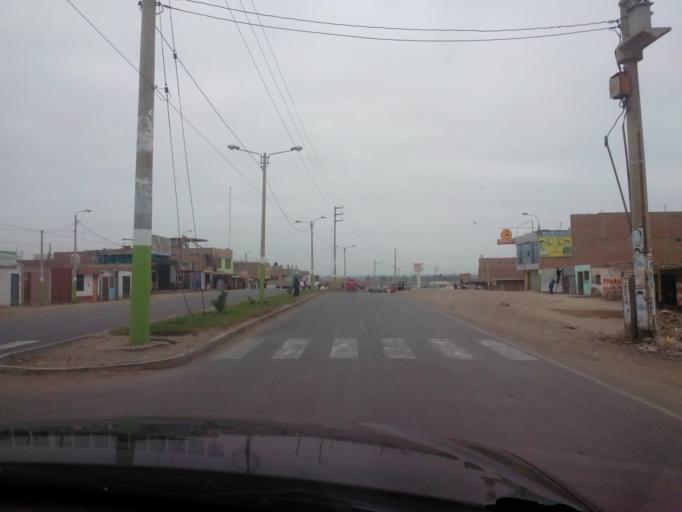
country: PE
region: Ica
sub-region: Provincia de Pisco
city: San Clemente
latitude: -13.6809
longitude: -76.1531
